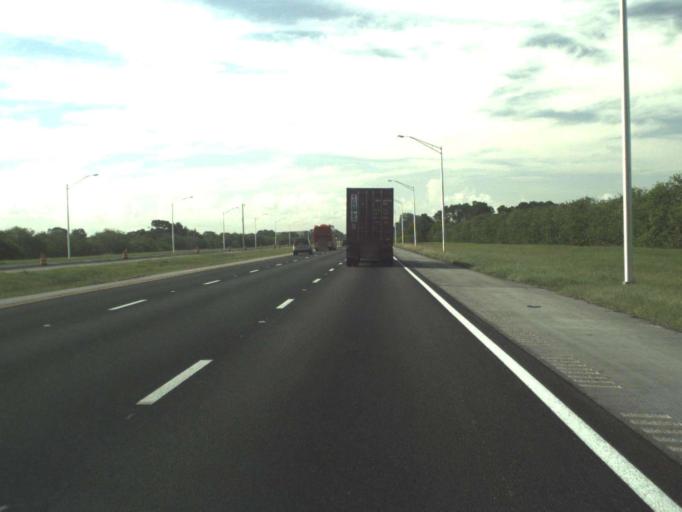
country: US
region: Florida
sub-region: Indian River County
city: West Vero Corridor
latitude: 27.6058
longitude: -80.5097
